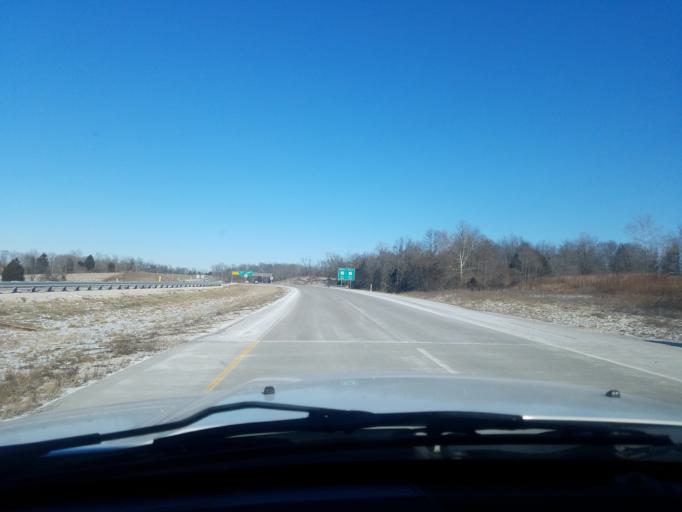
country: US
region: Indiana
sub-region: Monroe County
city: Bloomington
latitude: 39.1003
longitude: -86.5613
